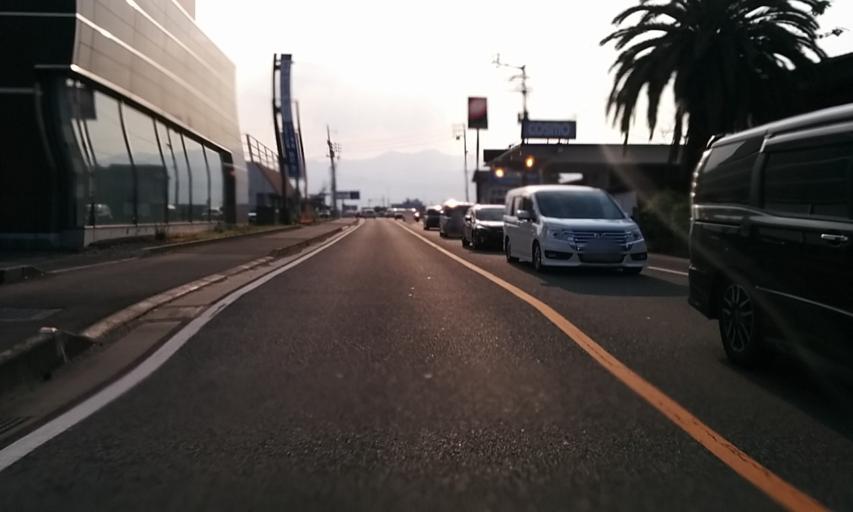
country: JP
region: Ehime
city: Saijo
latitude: 33.8973
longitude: 133.1112
